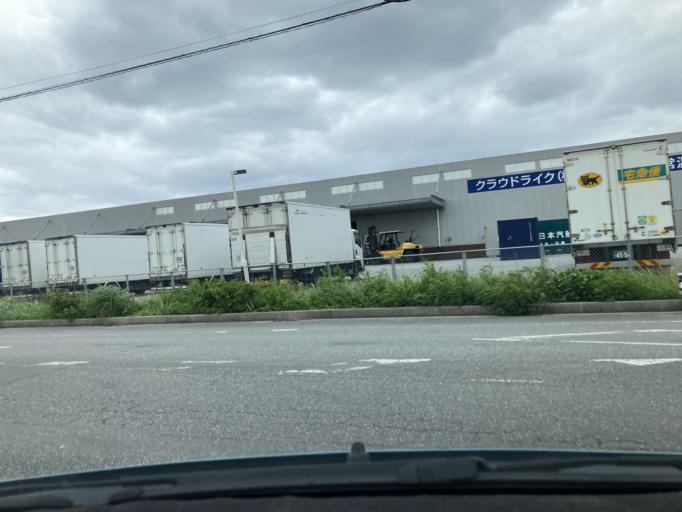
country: JP
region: Okinawa
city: Itoman
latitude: 26.1386
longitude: 127.6605
